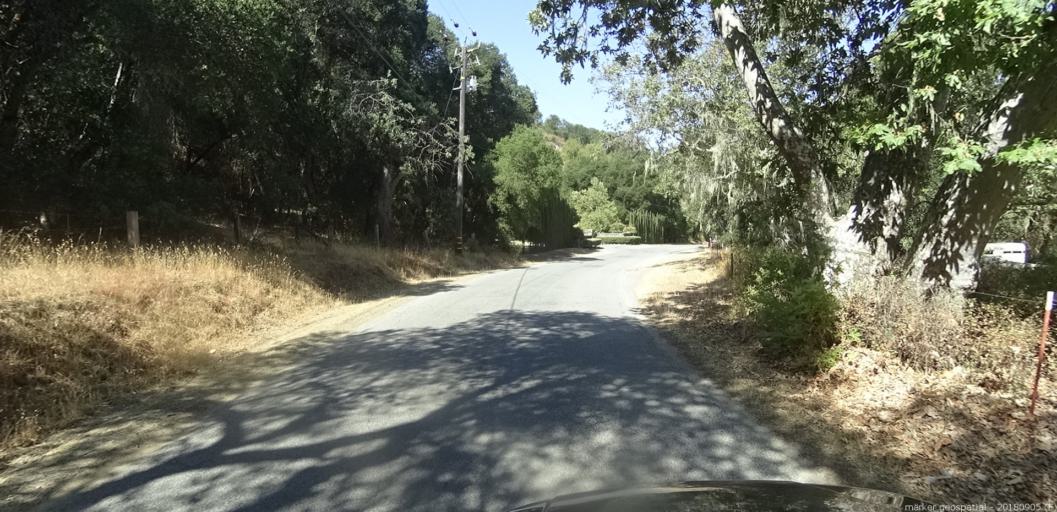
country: US
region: California
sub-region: Monterey County
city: Carmel Valley Village
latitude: 36.3913
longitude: -121.6228
